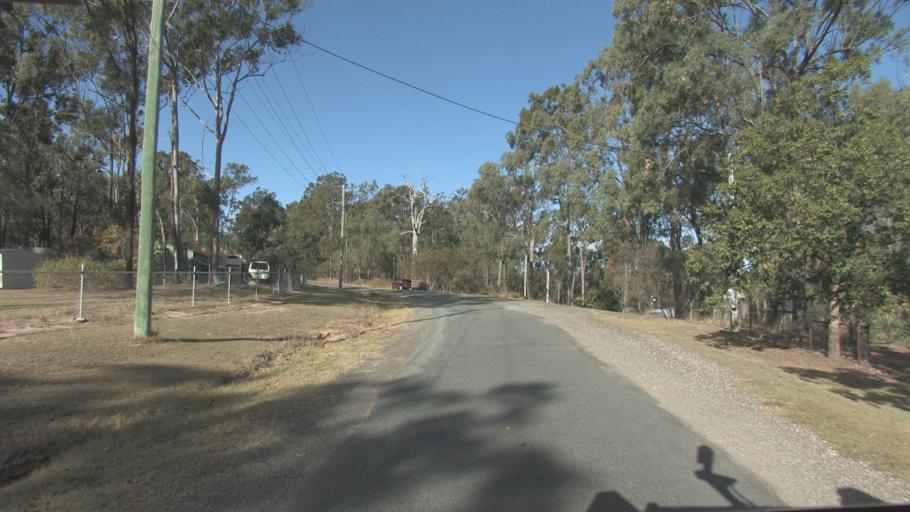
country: AU
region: Queensland
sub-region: Logan
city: Cedar Vale
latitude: -27.8470
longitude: 153.0647
